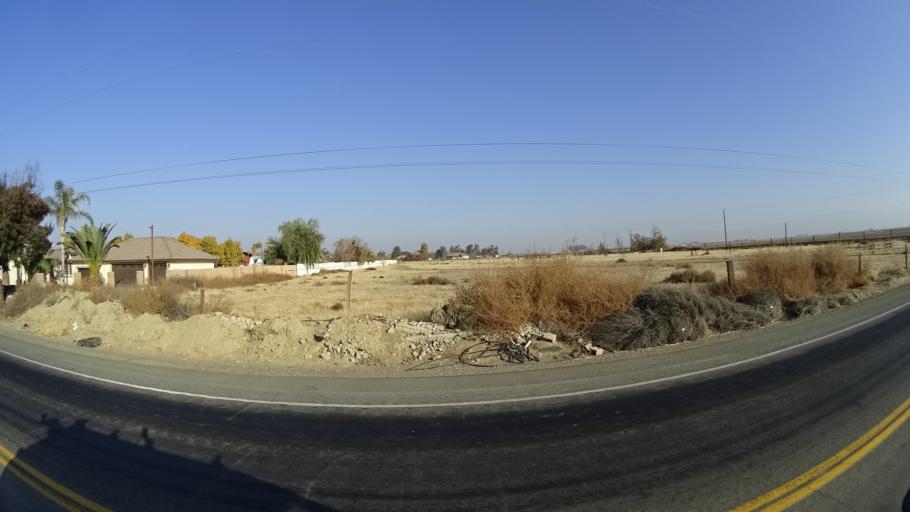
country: US
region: California
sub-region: Kern County
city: Weedpatch
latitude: 35.2377
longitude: -118.9615
